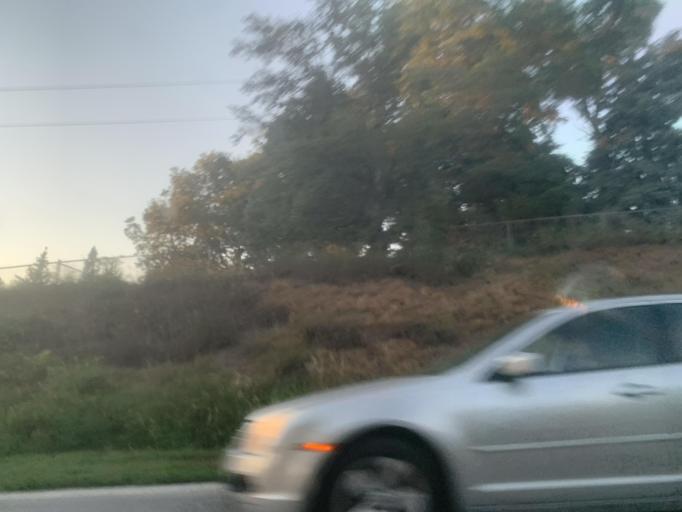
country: US
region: Nebraska
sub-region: Sarpy County
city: La Vista
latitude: 41.2052
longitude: -96.0007
